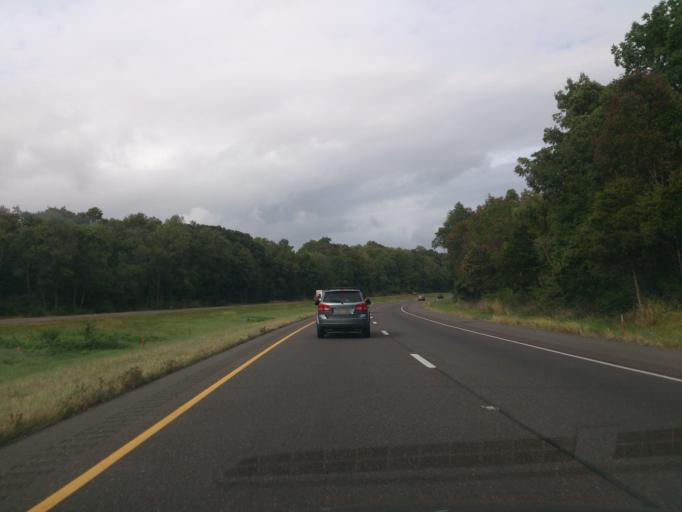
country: US
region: Pennsylvania
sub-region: Lancaster County
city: Ephrata
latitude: 40.1688
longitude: -76.1500
